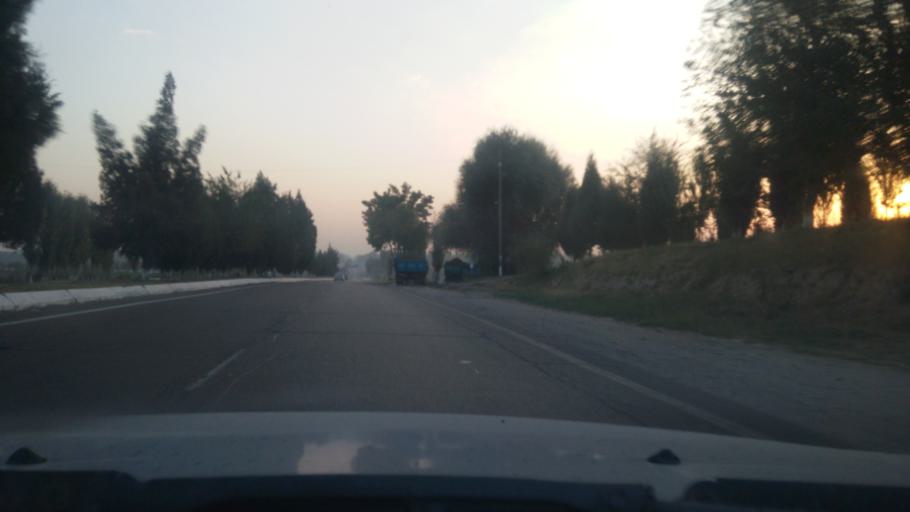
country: UZ
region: Toshkent
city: Amir Timur
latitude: 41.0455
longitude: 68.8884
